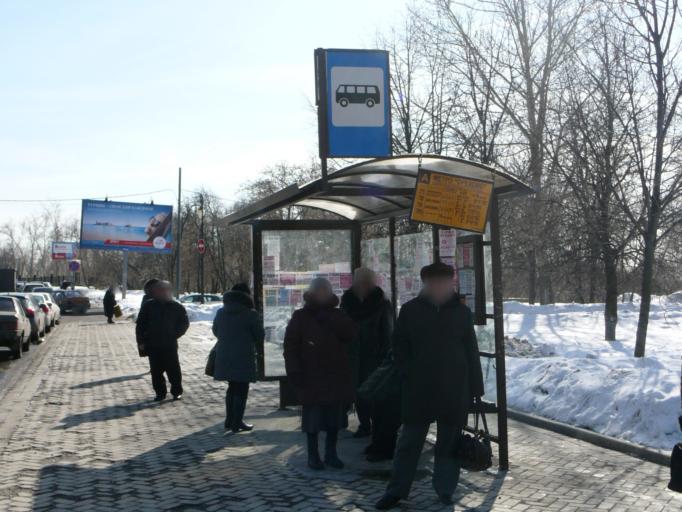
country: RU
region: Moscow
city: Orekhovo-Borisovo Severnoye
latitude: 55.6132
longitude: 37.6949
